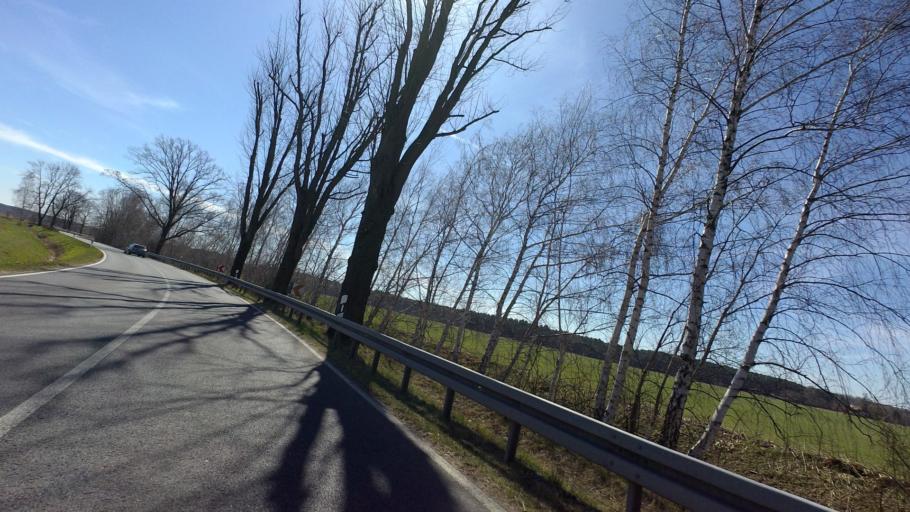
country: DE
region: Brandenburg
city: Mittenwalde
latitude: 52.2324
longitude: 13.5706
